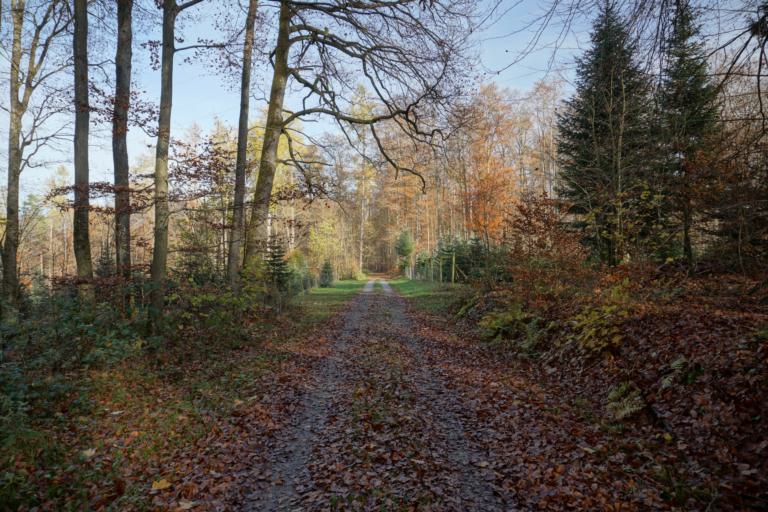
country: DE
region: Baden-Wuerttemberg
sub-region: Karlsruhe Region
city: Binau
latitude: 49.3243
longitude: 9.0424
